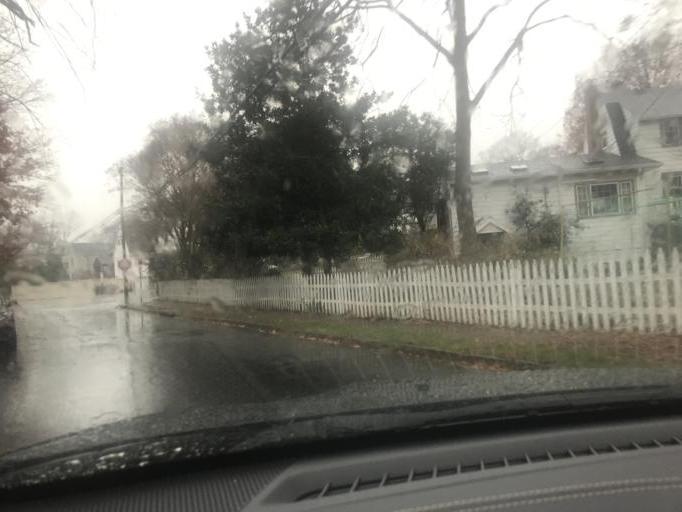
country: US
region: Virginia
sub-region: City of Alexandria
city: Alexandria
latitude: 38.8510
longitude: -77.0575
